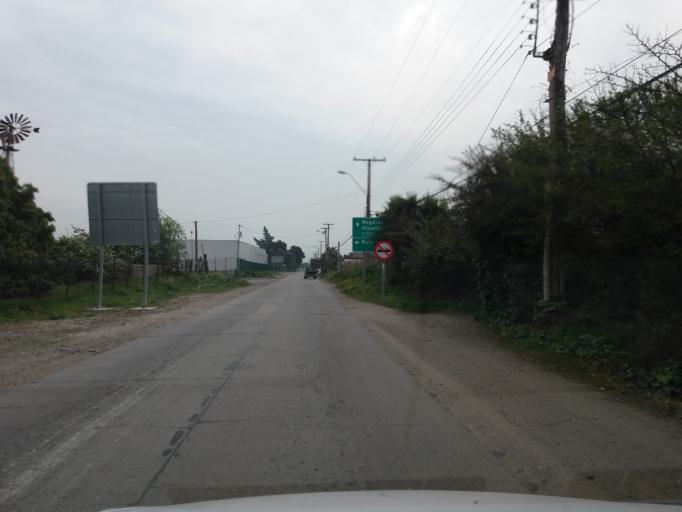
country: CL
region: Valparaiso
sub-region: Provincia de Quillota
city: Hacienda La Calera
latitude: -32.8400
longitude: -71.1051
